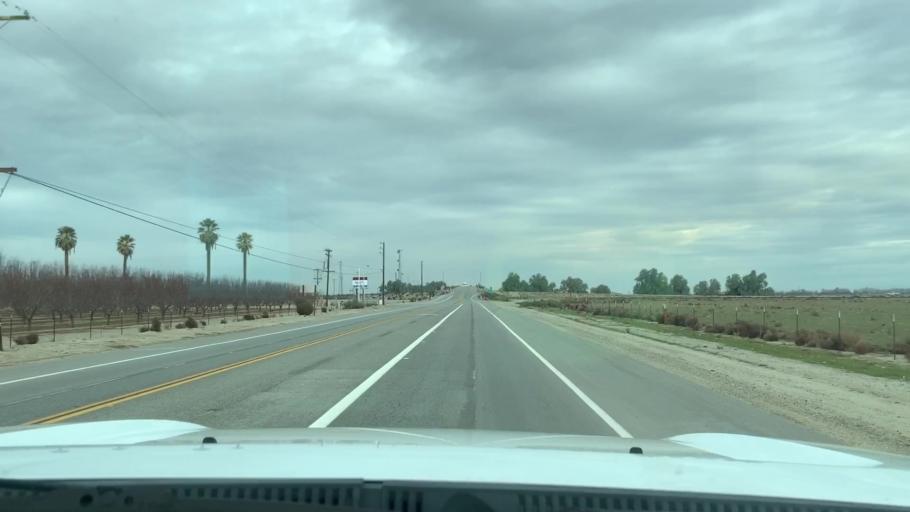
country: US
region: California
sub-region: Kern County
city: Rosedale
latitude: 35.2878
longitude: -119.2525
